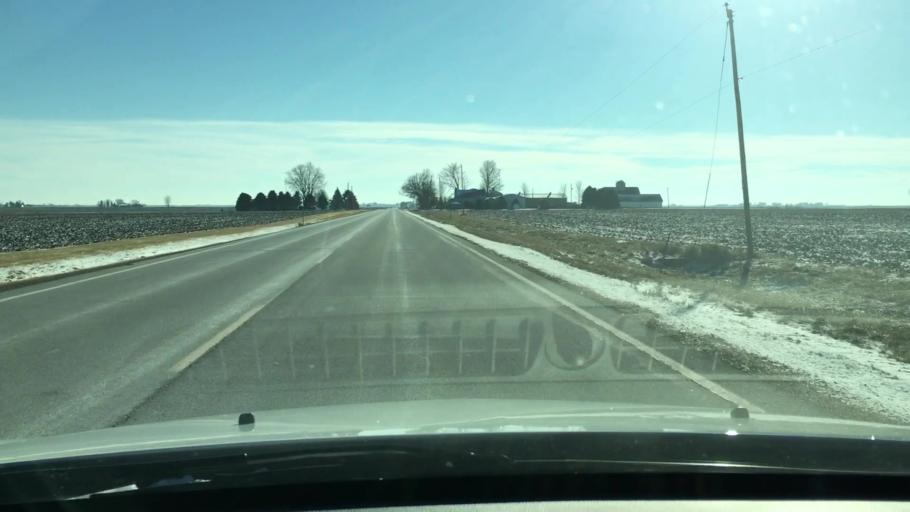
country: US
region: Illinois
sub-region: Ogle County
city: Rochelle
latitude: 41.8861
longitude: -89.0731
